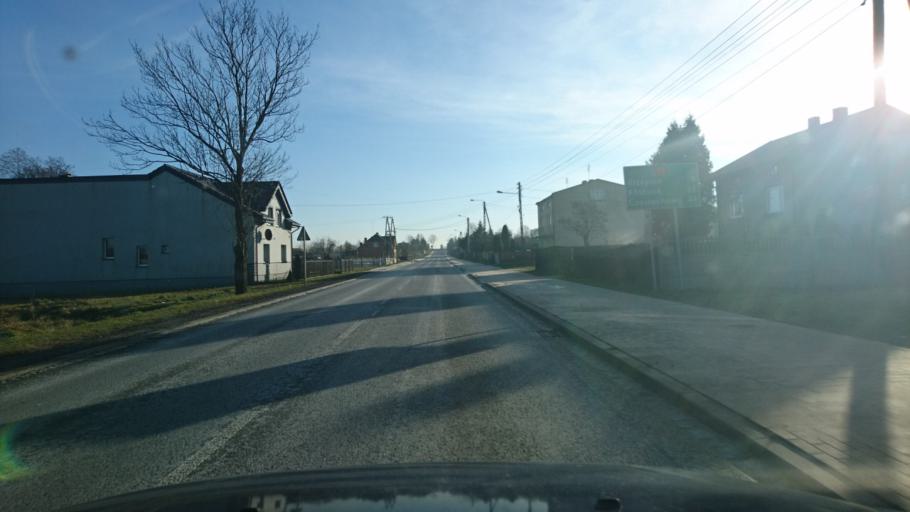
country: PL
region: Silesian Voivodeship
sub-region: Powiat klobucki
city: Starokrzepice
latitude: 51.0243
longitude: 18.6484
